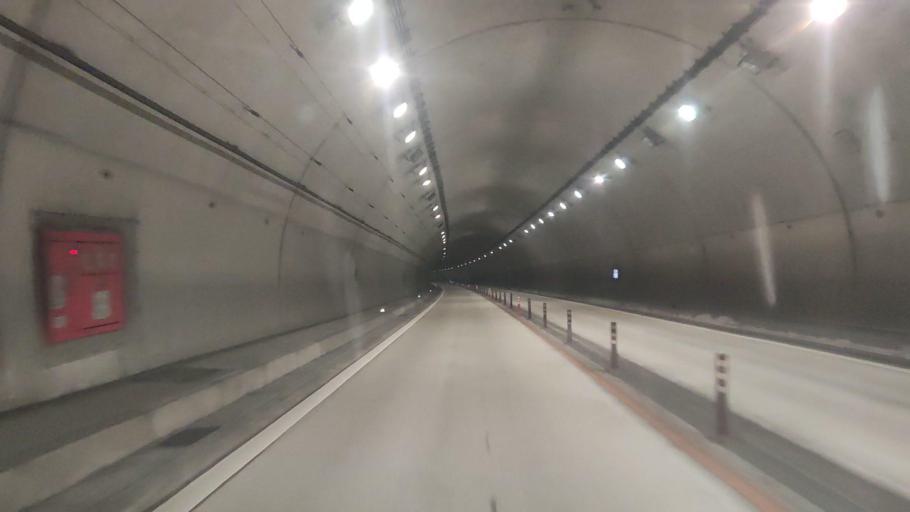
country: JP
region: Nagasaki
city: Shimabara
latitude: 32.7782
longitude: 130.3559
